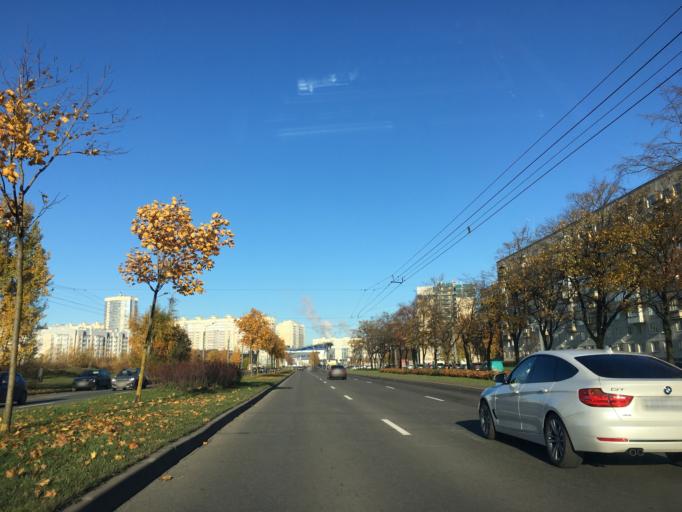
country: RU
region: St.-Petersburg
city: Uritsk
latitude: 59.8544
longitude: 30.1761
